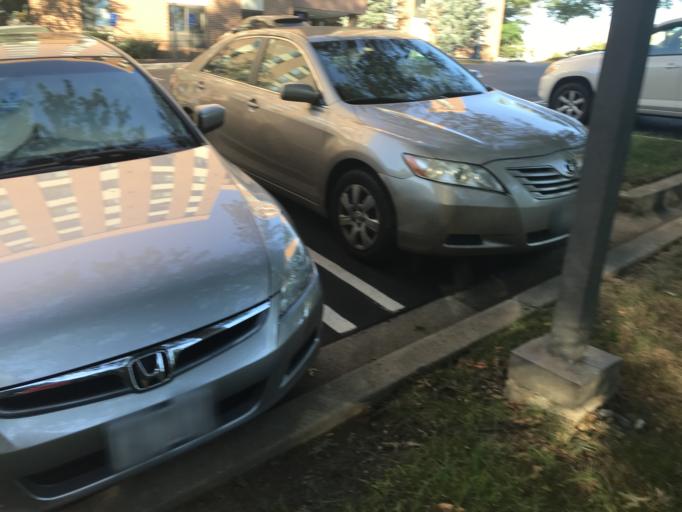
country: US
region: Maryland
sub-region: Montgomery County
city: Gaithersburg
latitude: 39.1495
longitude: -77.2042
